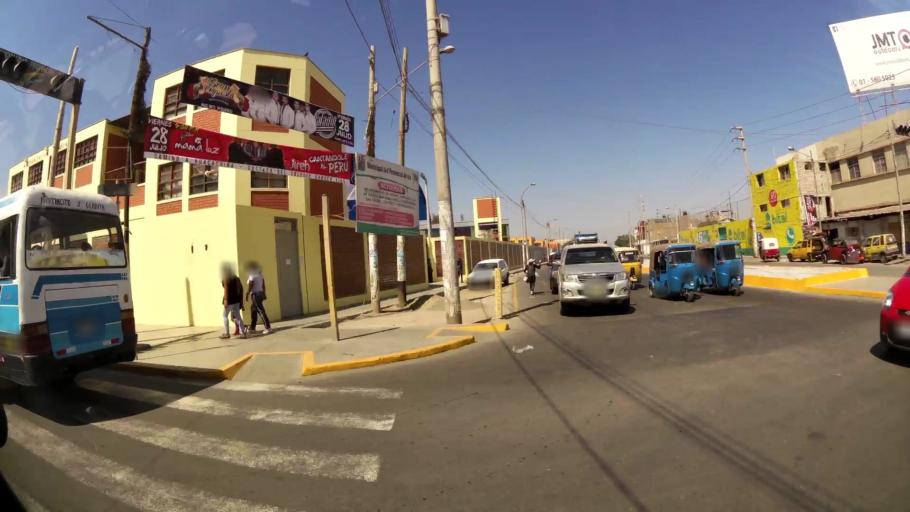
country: PE
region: Ica
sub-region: Provincia de Ica
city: Ica
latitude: -14.0653
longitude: -75.7355
